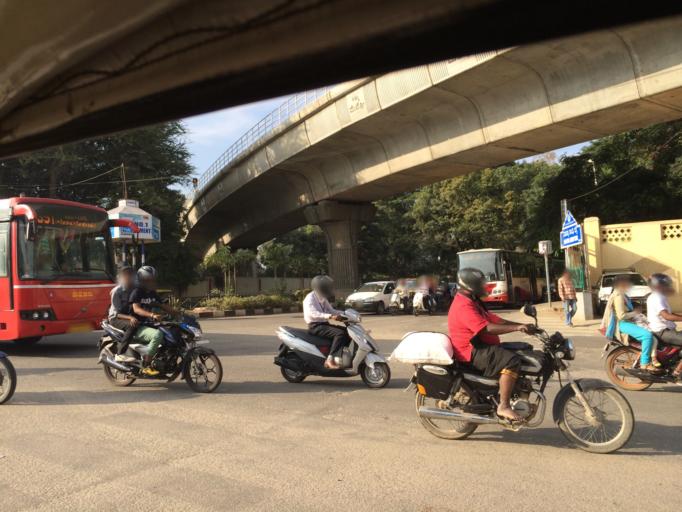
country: IN
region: Karnataka
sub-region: Bangalore Urban
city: Bangalore
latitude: 12.9766
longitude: 77.6020
